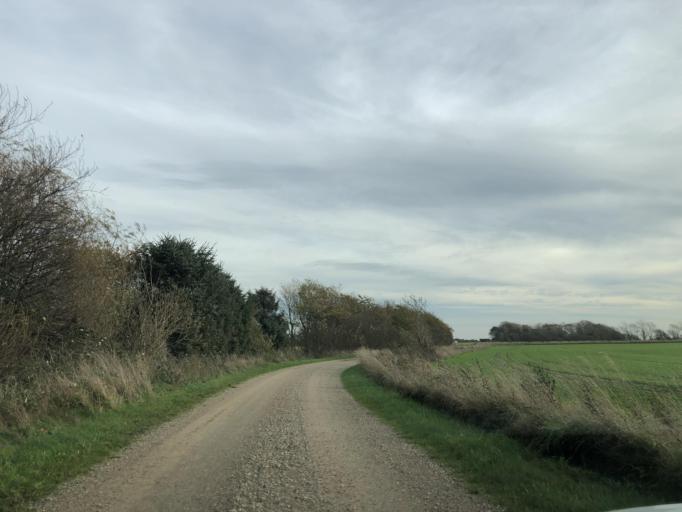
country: DK
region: South Denmark
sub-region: Tonder Kommune
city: Sherrebek
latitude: 55.1813
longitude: 8.7006
